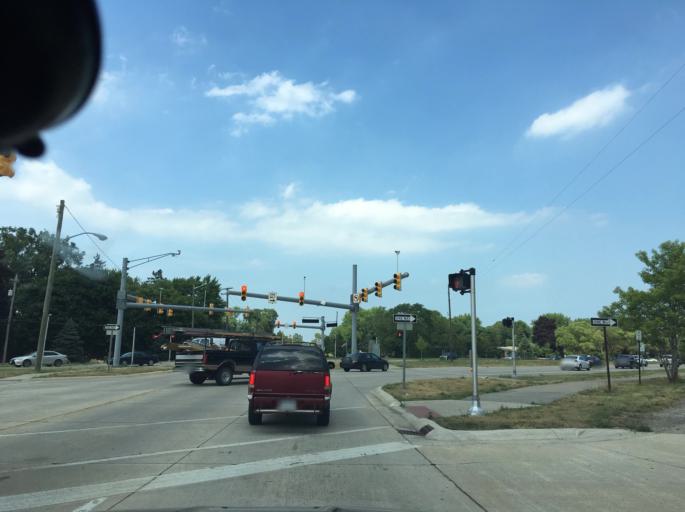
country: US
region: Michigan
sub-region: Macomb County
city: Clinton
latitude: 42.5681
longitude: -82.9395
